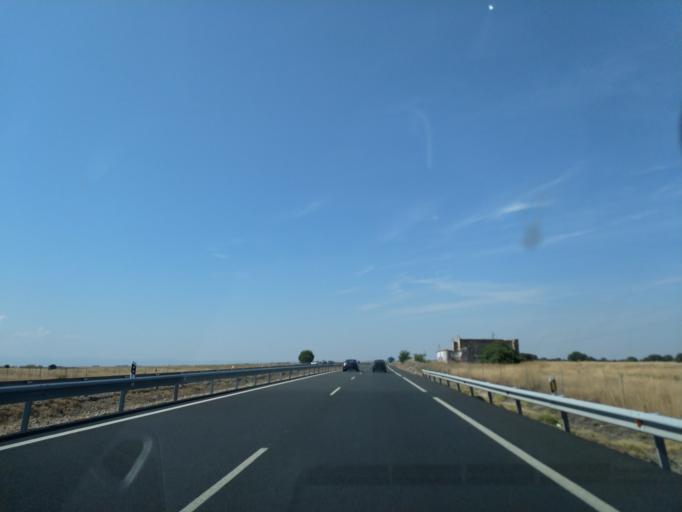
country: ES
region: Castille-La Mancha
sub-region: Province of Toledo
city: Velada
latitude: 39.9319
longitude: -5.0046
